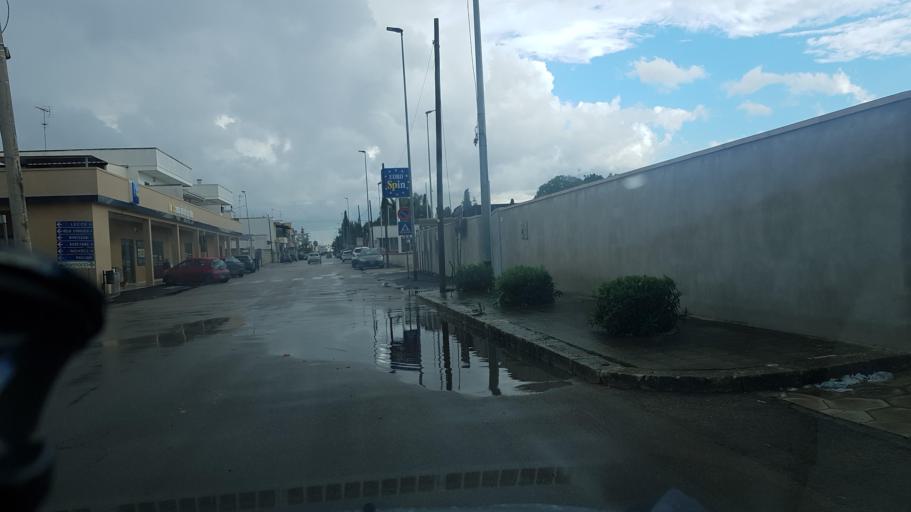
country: IT
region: Apulia
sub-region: Provincia di Lecce
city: Carmiano
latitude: 40.3382
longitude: 18.0423
